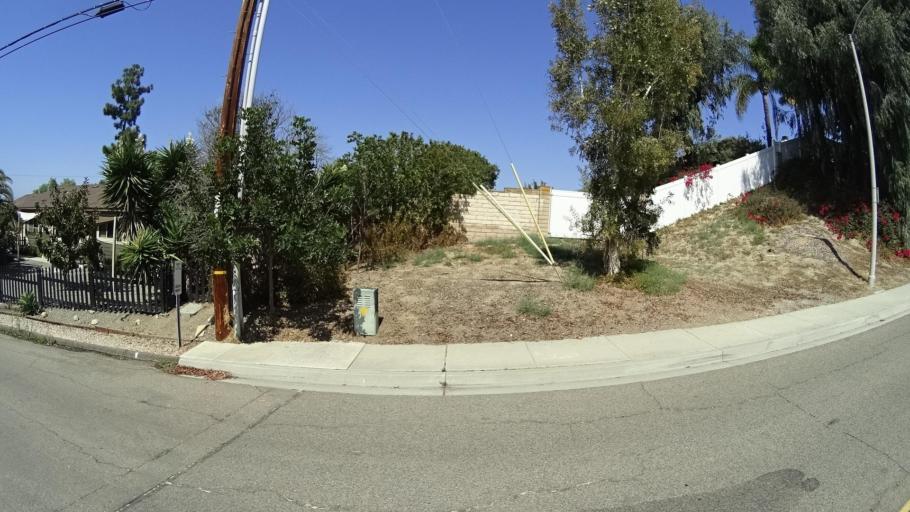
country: US
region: California
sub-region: San Diego County
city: Lake San Marcos
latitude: 33.1593
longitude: -117.2166
